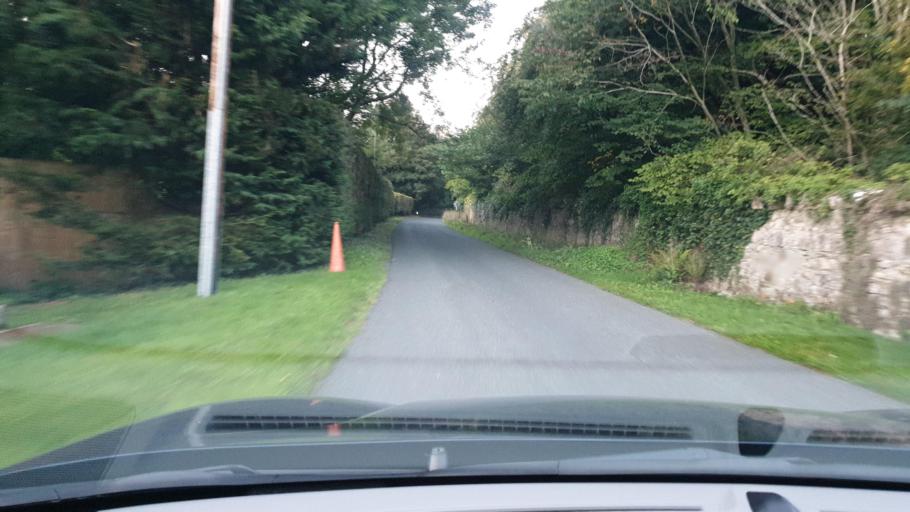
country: IE
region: Leinster
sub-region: Kildare
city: Prosperous
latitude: 53.3441
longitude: -6.7578
